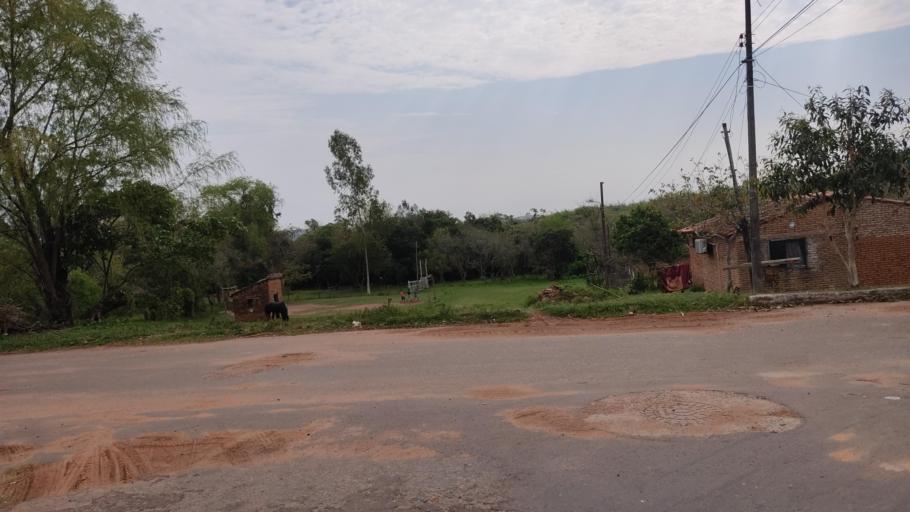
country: PY
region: Misiones
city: San Juan Bautista
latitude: -26.6627
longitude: -57.1481
